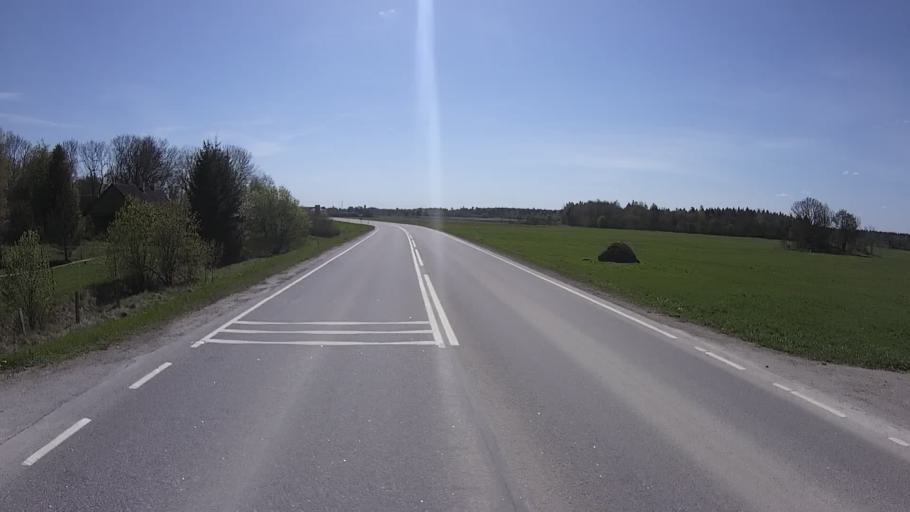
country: EE
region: Harju
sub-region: Keila linn
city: Keila
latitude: 59.3135
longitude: 24.3169
